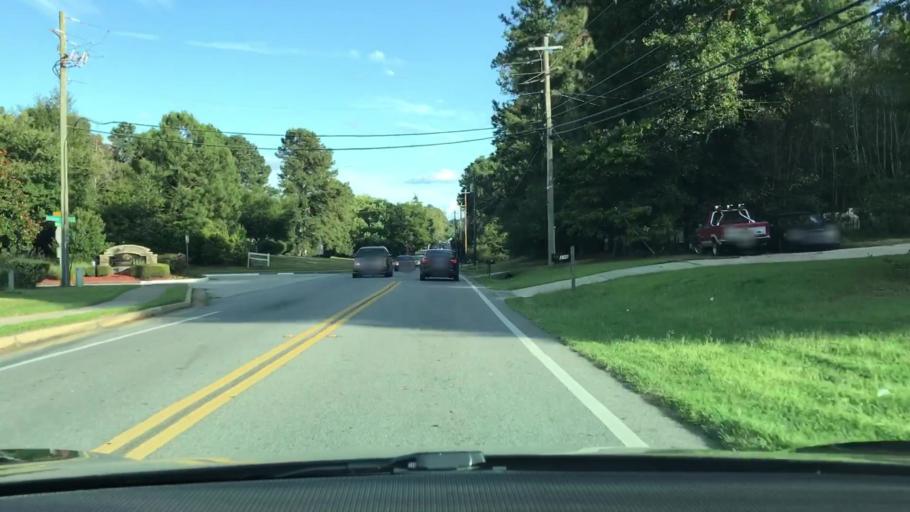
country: US
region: Georgia
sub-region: Gwinnett County
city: Dacula
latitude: 33.9972
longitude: -83.9033
